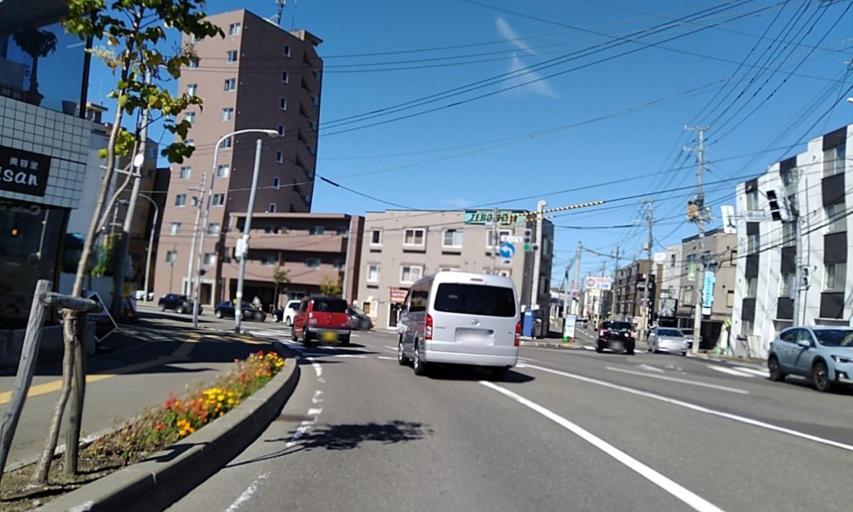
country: JP
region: Hokkaido
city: Sapporo
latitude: 43.0150
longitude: 141.3686
